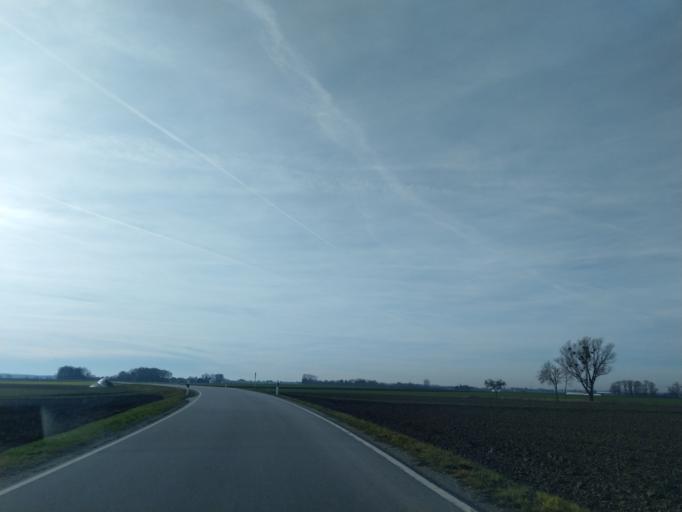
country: DE
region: Bavaria
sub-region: Lower Bavaria
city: Otzing
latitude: 48.7374
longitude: 12.7971
